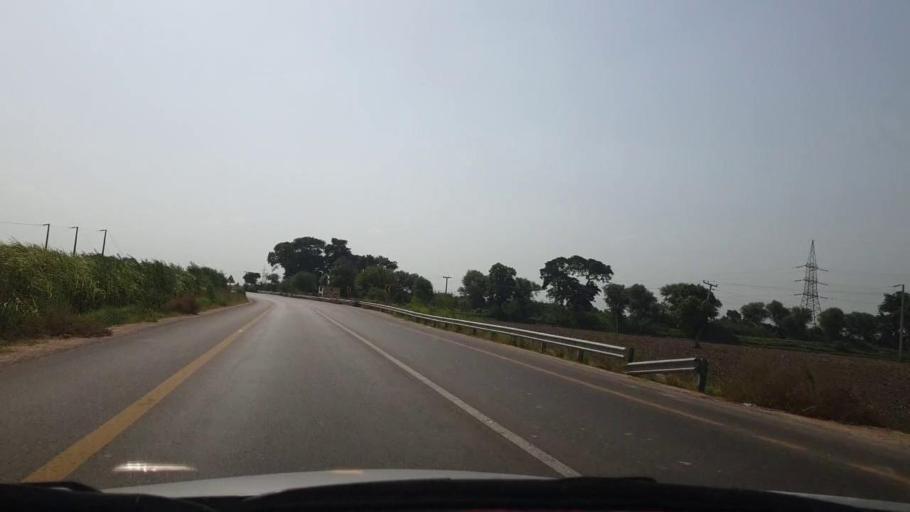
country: PK
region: Sindh
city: Matli
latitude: 25.0817
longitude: 68.6084
